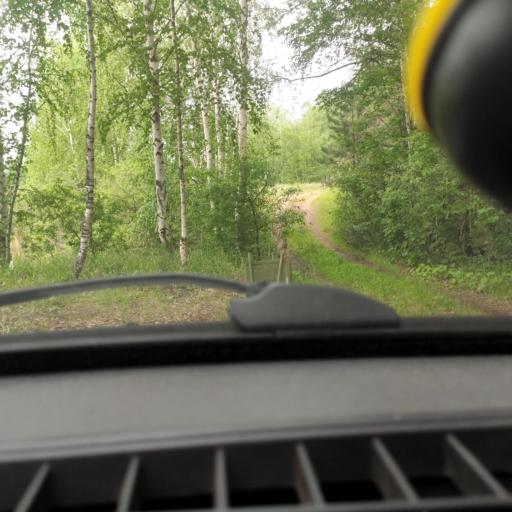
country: RU
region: Samara
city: Zhigulevsk
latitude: 53.5032
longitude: 49.5002
